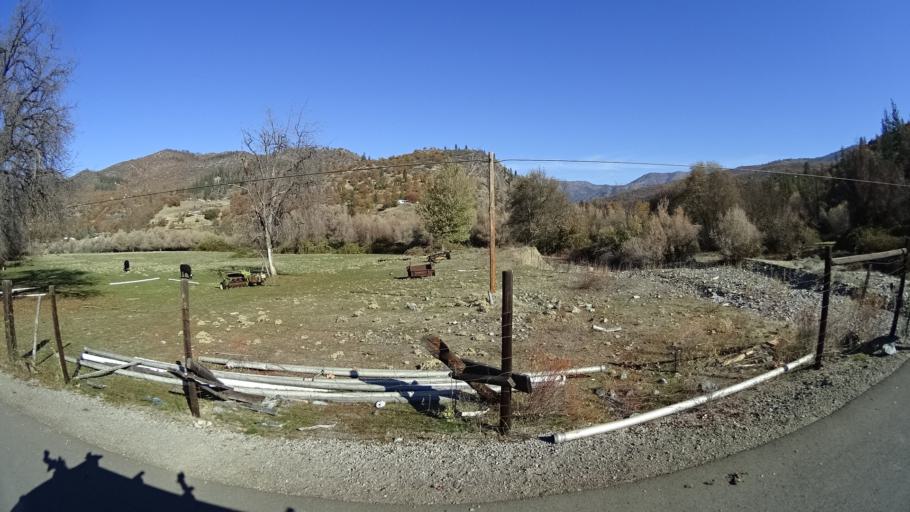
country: US
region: California
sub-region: Siskiyou County
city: Yreka
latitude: 41.8302
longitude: -122.8473
